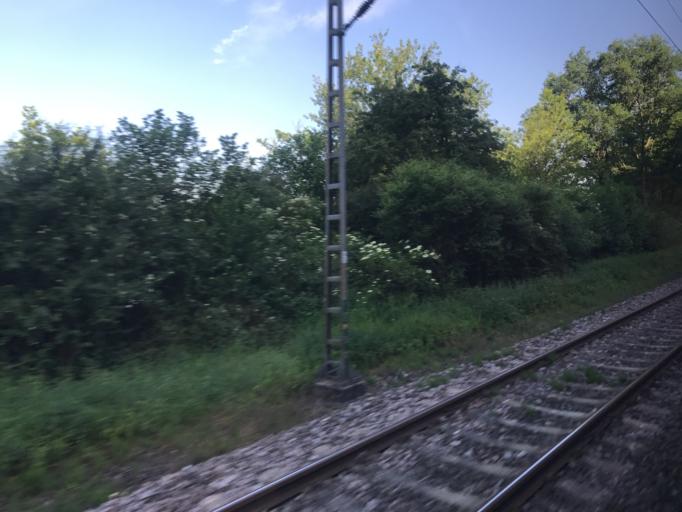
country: DE
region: Saarland
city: Sankt Wendel
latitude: 49.4896
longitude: 7.1691
